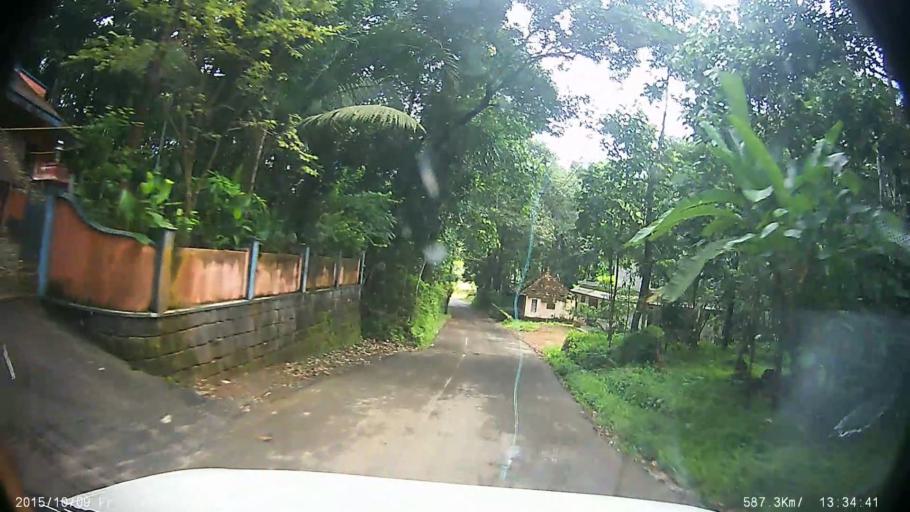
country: IN
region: Kerala
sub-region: Ernakulam
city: Ramamangalam
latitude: 9.9044
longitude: 76.5573
